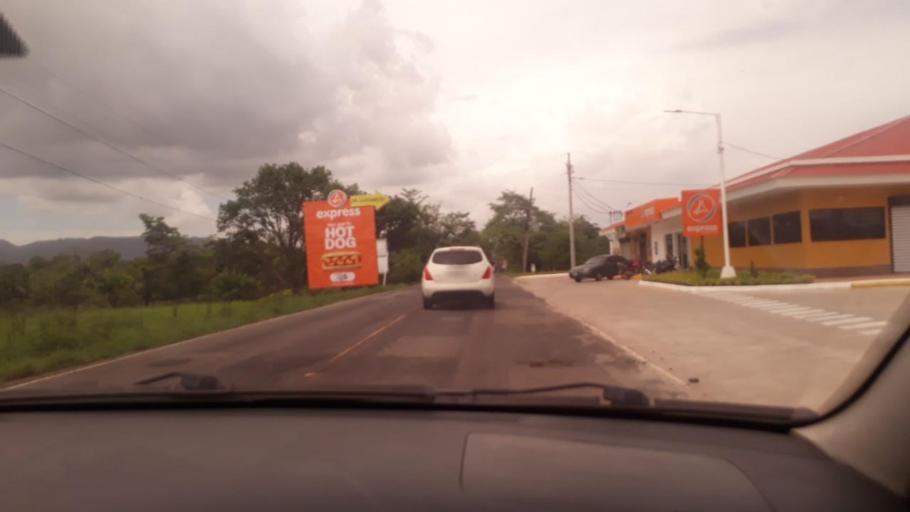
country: GT
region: Jutiapa
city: Jutiapa
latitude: 14.2816
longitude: -89.9553
